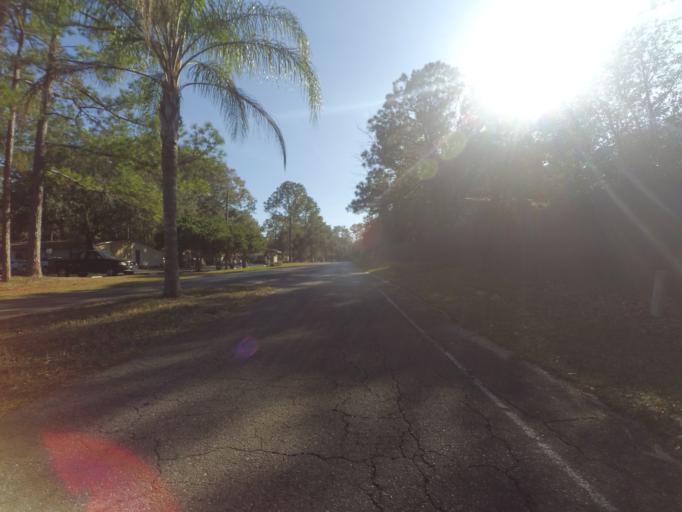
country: US
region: Florida
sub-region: Alachua County
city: Gainesville
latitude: 29.6193
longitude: -82.3575
